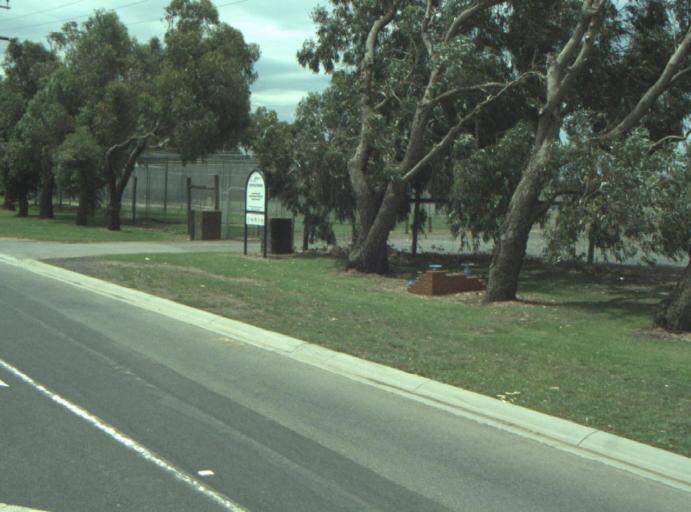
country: AU
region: Victoria
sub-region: Greater Geelong
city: Leopold
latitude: -38.1852
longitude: 144.4558
